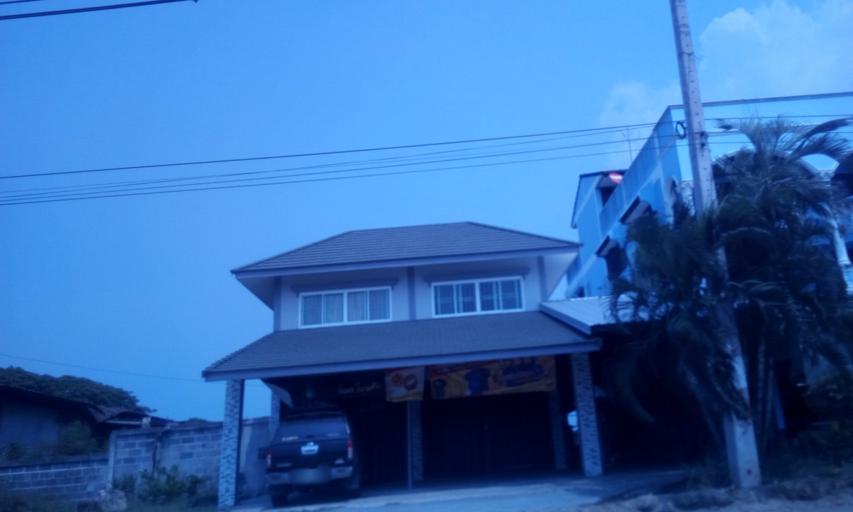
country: TH
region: Chon Buri
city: Phanat Nikhom
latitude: 13.3717
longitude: 101.1953
